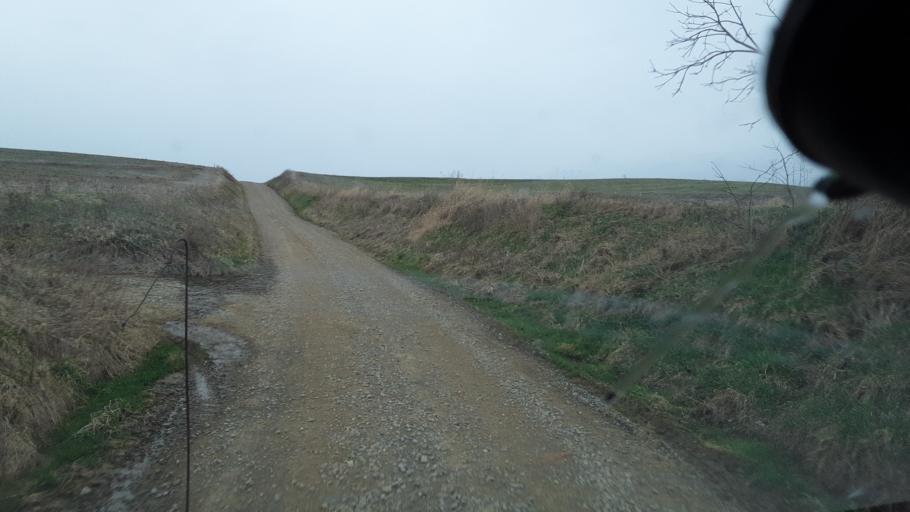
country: US
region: Ohio
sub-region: Coshocton County
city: West Lafayette
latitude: 40.3377
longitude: -81.6967
